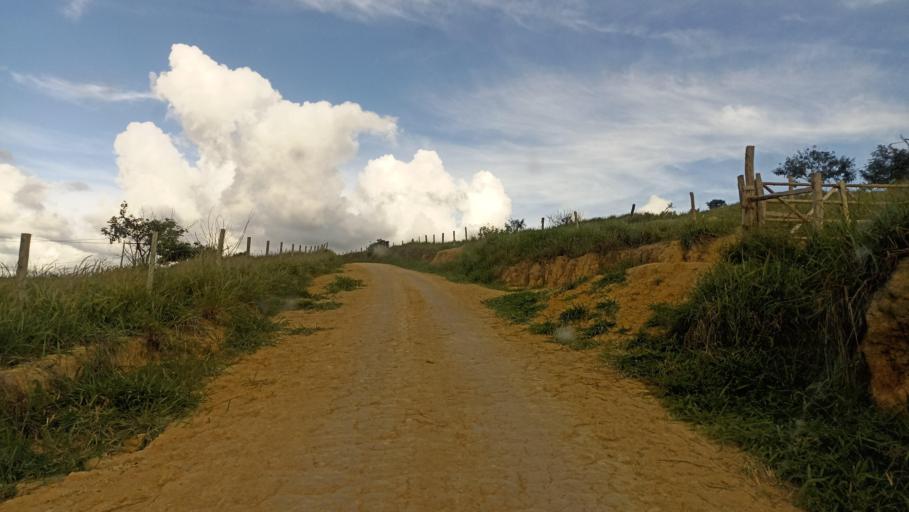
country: BR
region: Minas Gerais
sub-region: Almenara
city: Almenara
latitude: -16.5489
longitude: -40.4562
